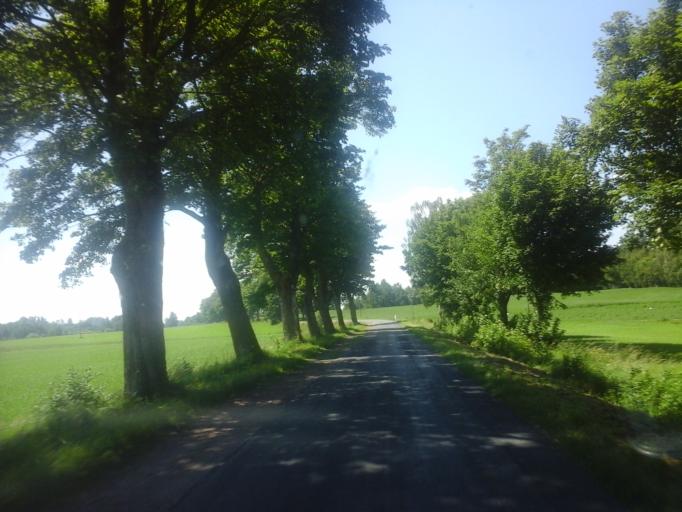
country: PL
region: West Pomeranian Voivodeship
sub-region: Powiat bialogardzki
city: Bialogard
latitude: 54.0711
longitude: 16.0400
